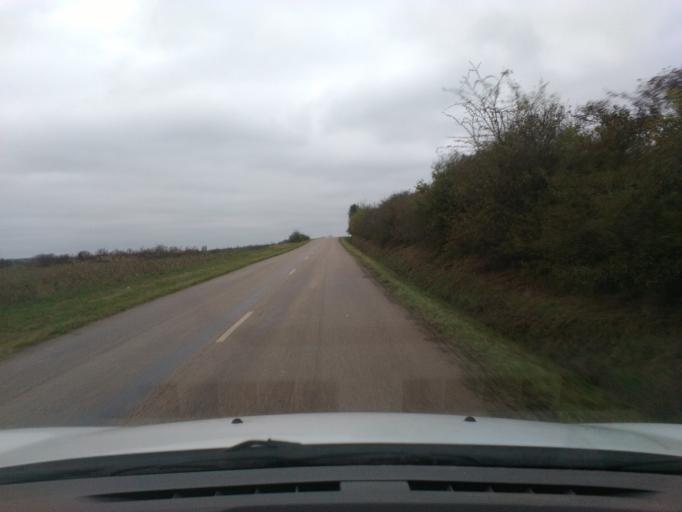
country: FR
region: Lorraine
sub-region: Departement des Vosges
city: Aydoilles
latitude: 48.2532
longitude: 6.5797
